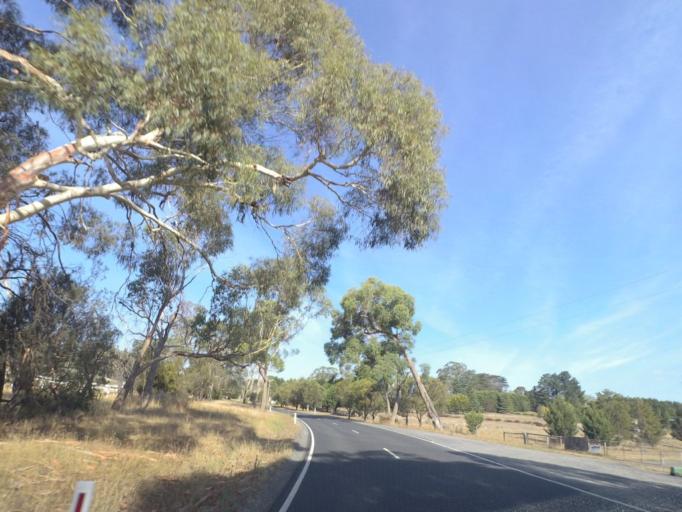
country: AU
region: Victoria
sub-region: Yarra Ranges
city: Mount Evelyn
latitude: -37.7275
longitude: 145.4310
